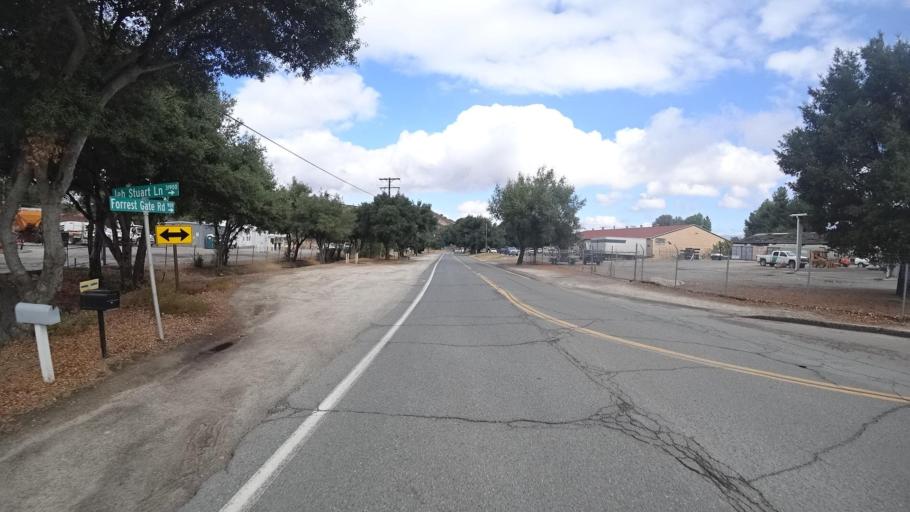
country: US
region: California
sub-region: San Diego County
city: Campo
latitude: 32.6069
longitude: -116.4724
